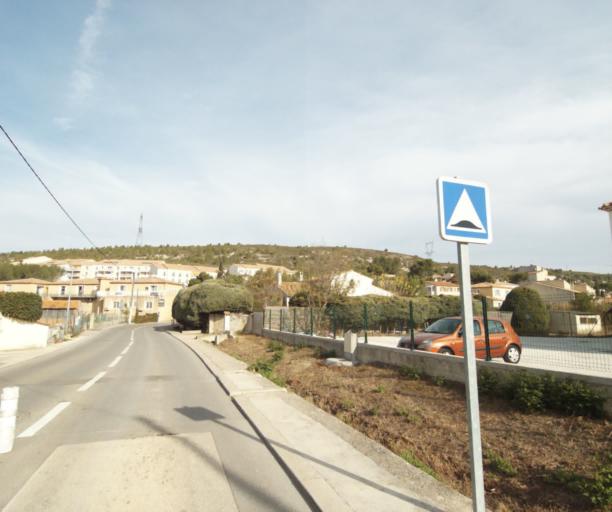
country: FR
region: Provence-Alpes-Cote d'Azur
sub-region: Departement des Bouches-du-Rhone
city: Ensues-la-Redonne
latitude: 43.3544
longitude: 5.1974
